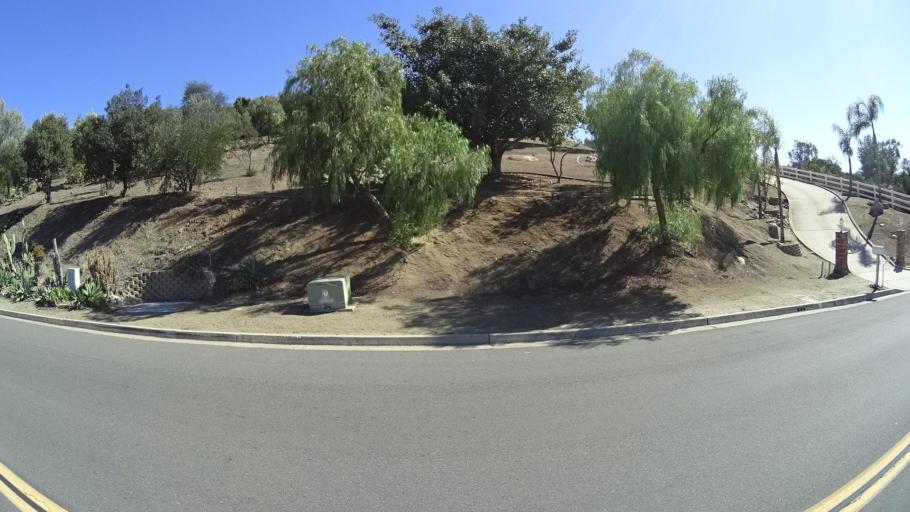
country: US
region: California
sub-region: San Diego County
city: Harbison Canyon
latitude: 32.8696
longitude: -116.8514
